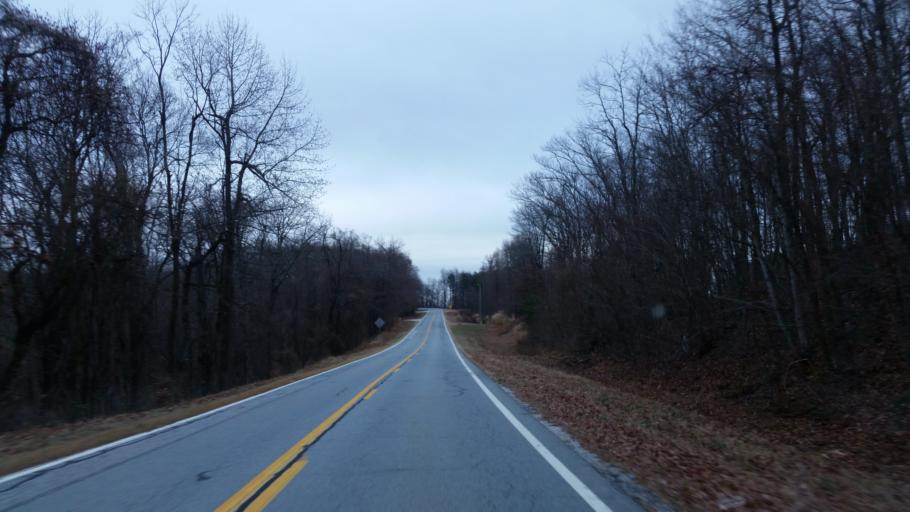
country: US
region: Georgia
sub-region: Pickens County
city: Jasper
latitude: 34.5430
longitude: -84.3359
